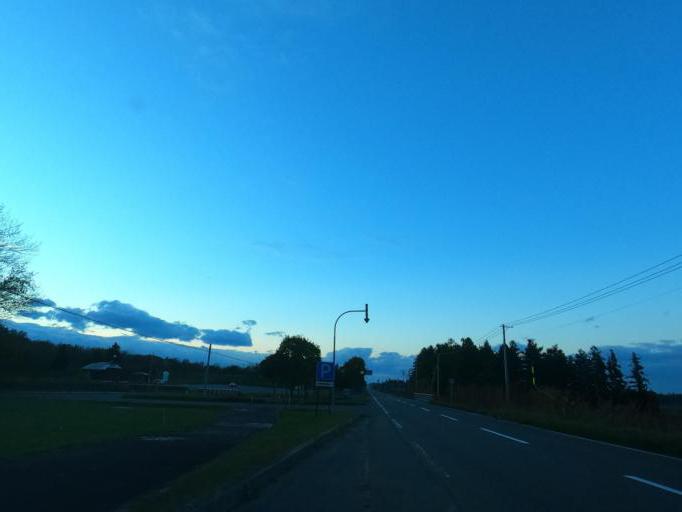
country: JP
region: Hokkaido
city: Obihiro
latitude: 42.6394
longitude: 143.2050
